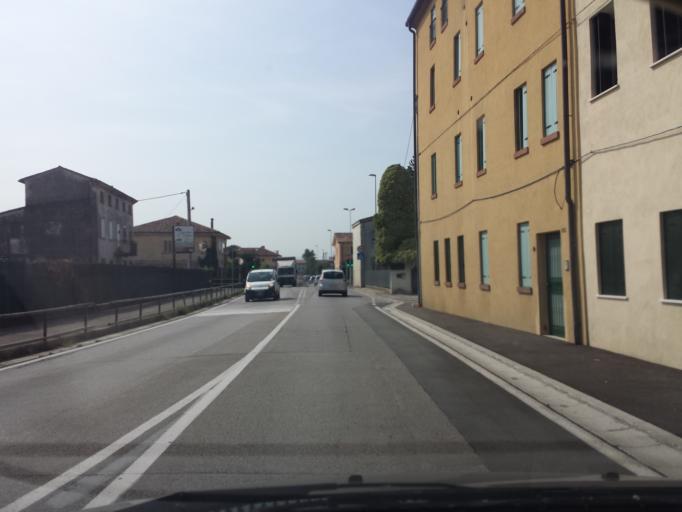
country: IT
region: Veneto
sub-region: Provincia di Vicenza
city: Monticello Conte Otto
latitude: 45.5769
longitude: 11.5516
